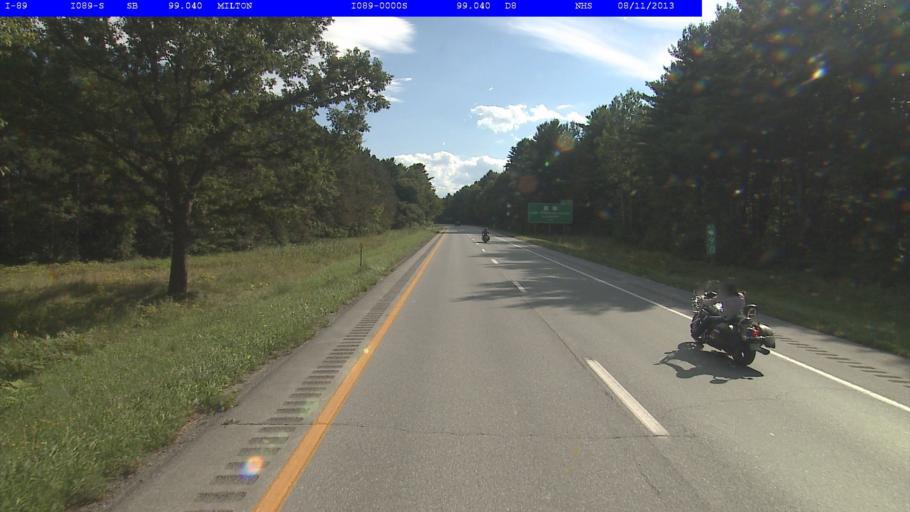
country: US
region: Vermont
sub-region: Chittenden County
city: Colchester
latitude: 44.6062
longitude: -73.1699
